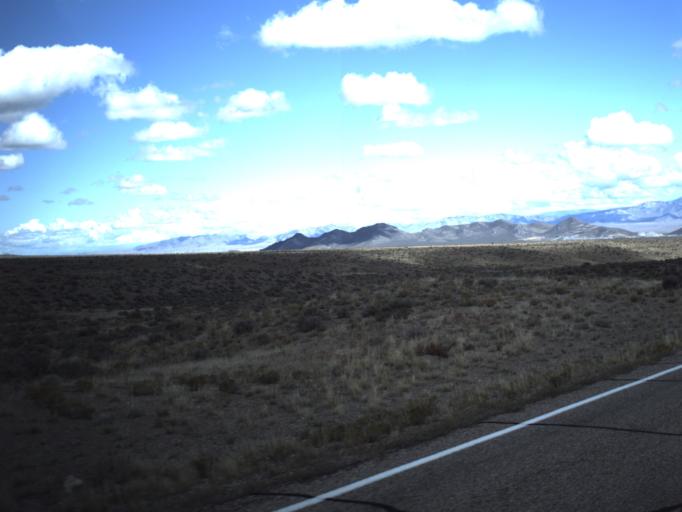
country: US
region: Utah
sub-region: Beaver County
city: Milford
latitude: 38.4408
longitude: -113.1629
